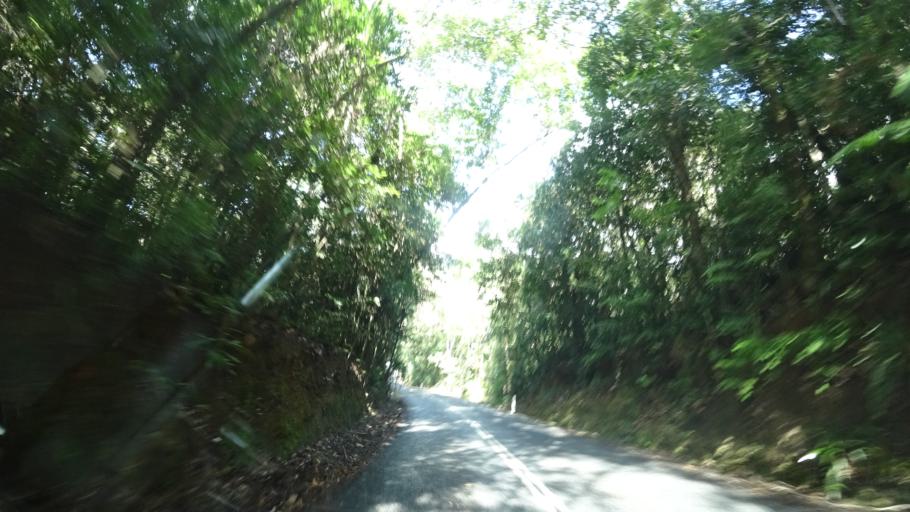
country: AU
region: Queensland
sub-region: Cairns
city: Port Douglas
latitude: -16.1382
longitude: 145.4310
